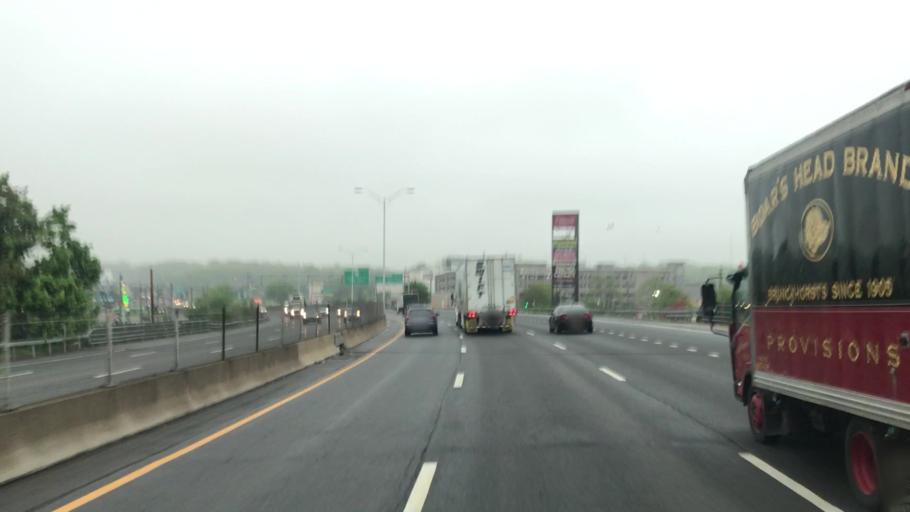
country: US
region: New York
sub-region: Westchester County
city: Mount Vernon
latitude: 40.9250
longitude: -73.8585
